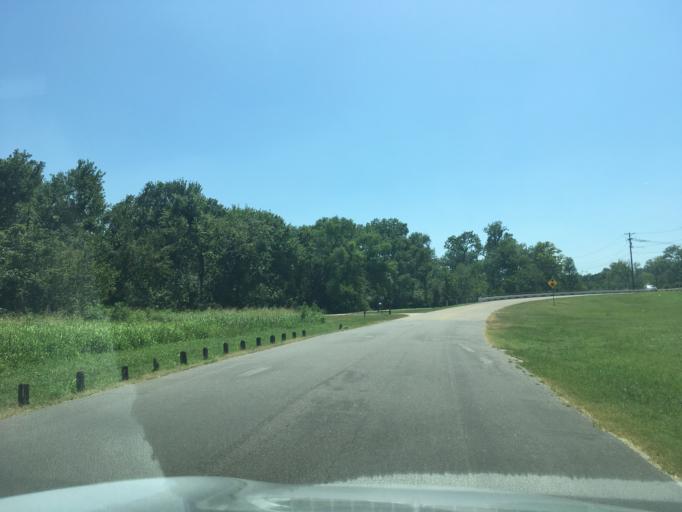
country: US
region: Texas
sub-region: Dallas County
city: Highland Park
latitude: 32.8586
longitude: -96.7224
